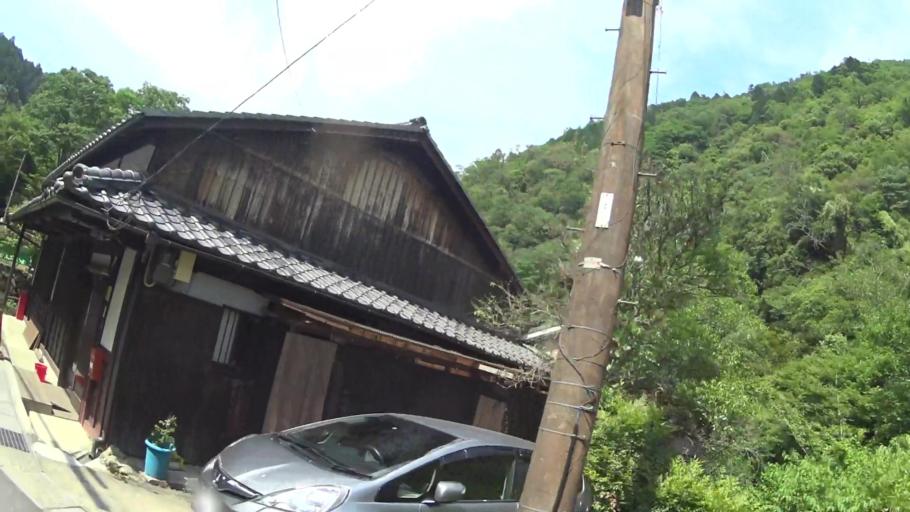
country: JP
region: Kyoto
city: Kameoka
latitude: 35.0390
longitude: 135.6576
